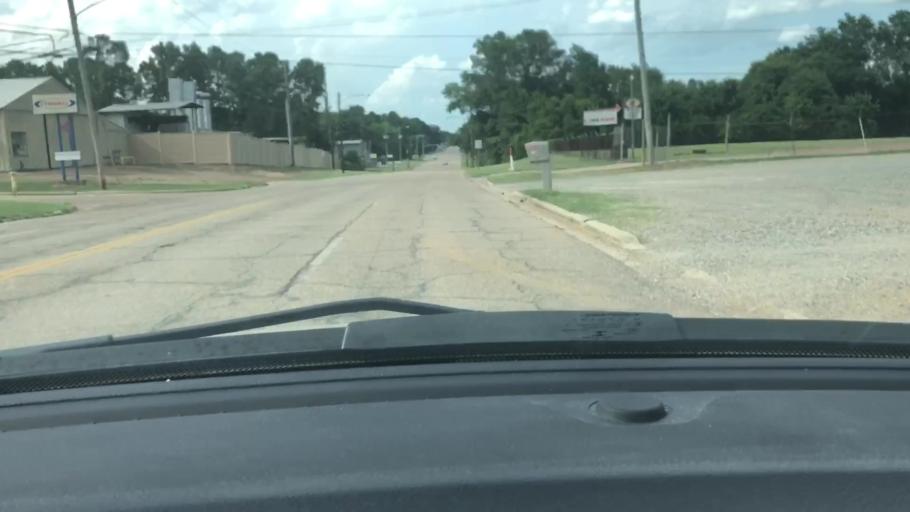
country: US
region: Texas
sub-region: Bowie County
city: Wake Village
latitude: 33.4162
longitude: -94.0803
